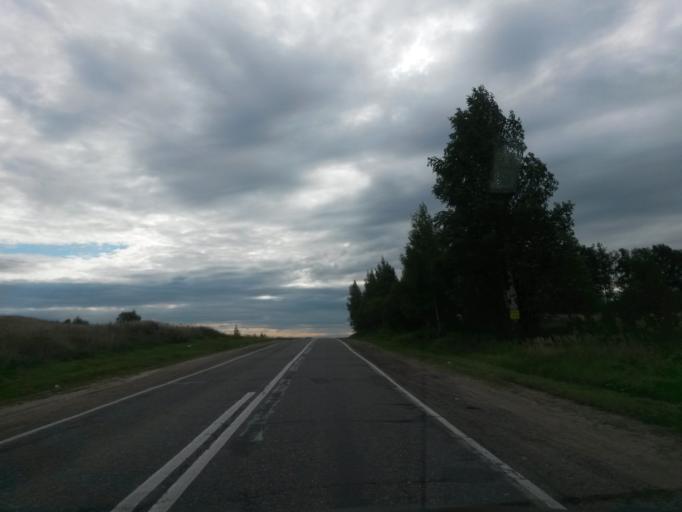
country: RU
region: Jaroslavl
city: Gavrilov-Yam
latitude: 57.3599
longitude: 39.7737
